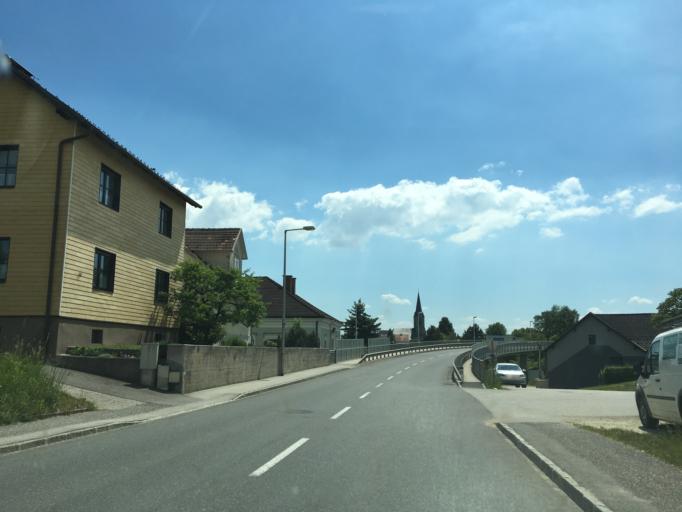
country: AT
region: Upper Austria
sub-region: Politischer Bezirk Urfahr-Umgebung
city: Engerwitzdorf
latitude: 48.3594
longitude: 14.5331
